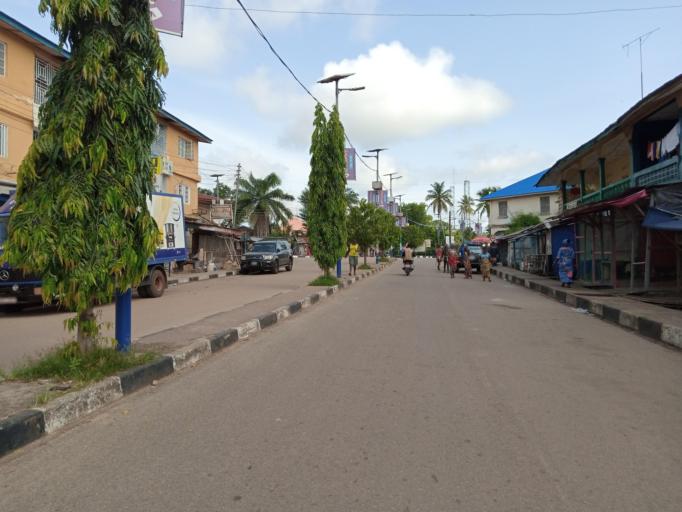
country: SL
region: Southern Province
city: Bo
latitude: 7.9665
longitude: -11.7402
